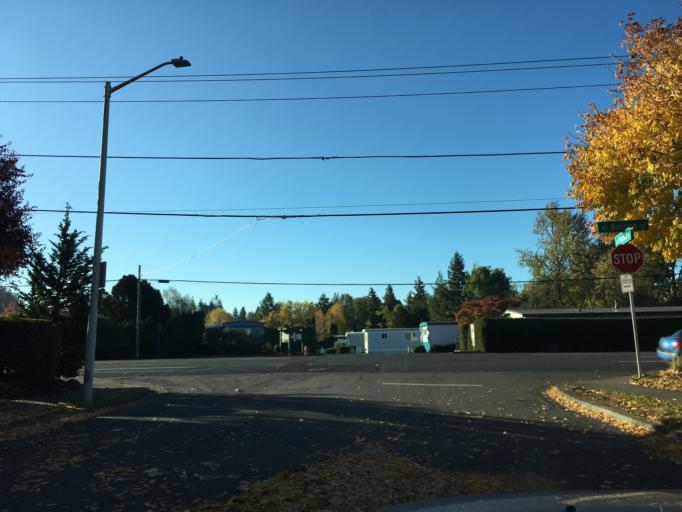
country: US
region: Oregon
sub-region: Multnomah County
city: Gresham
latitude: 45.5052
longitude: -122.4031
